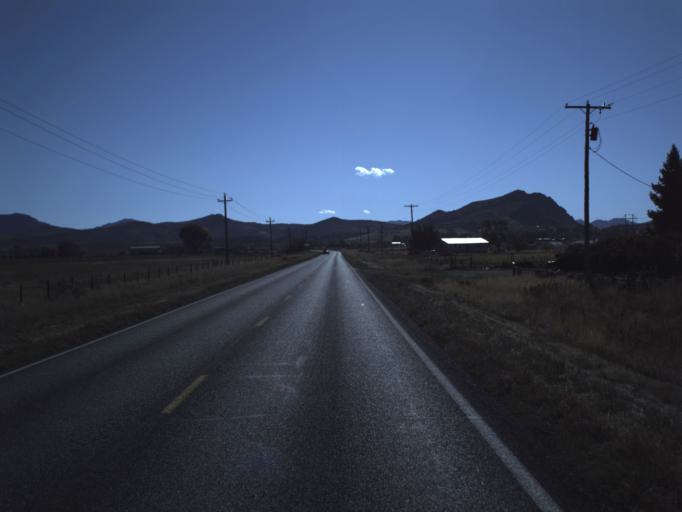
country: US
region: Utah
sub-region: Washington County
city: Enterprise
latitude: 37.6754
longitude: -113.5616
